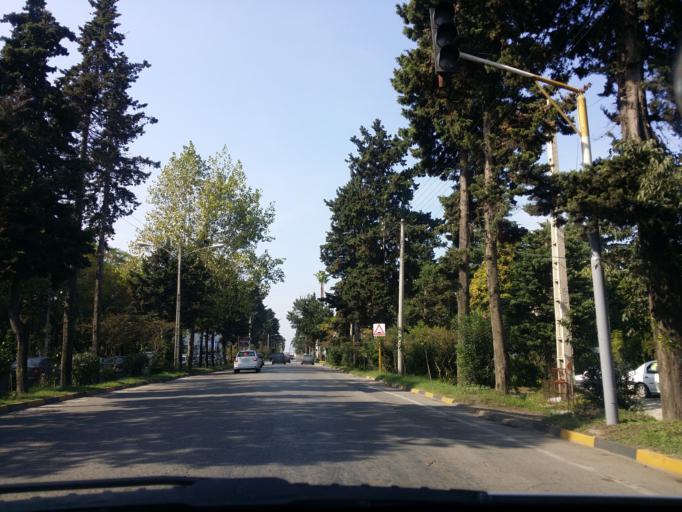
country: IR
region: Mazandaran
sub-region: Nowshahr
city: Nowshahr
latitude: 36.6548
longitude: 51.4927
